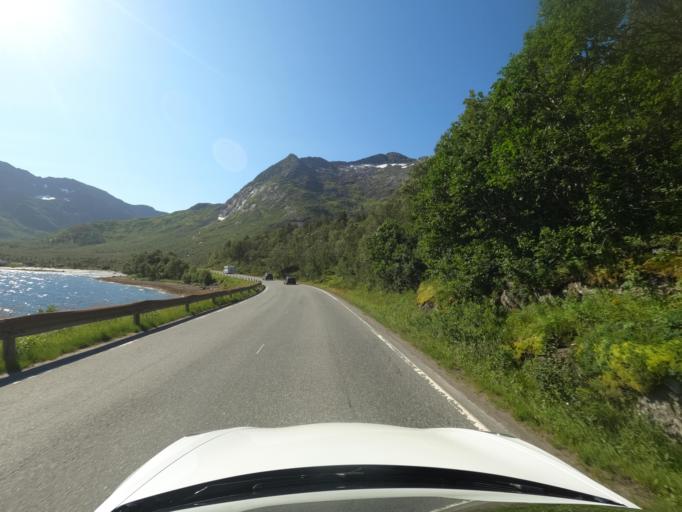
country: NO
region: Nordland
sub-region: Lodingen
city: Lodingen
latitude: 68.5372
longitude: 15.7224
